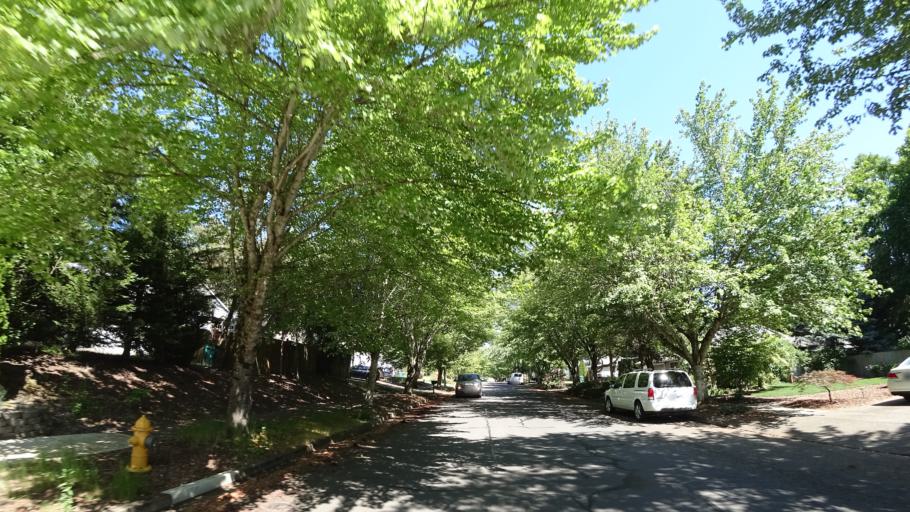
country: US
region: Oregon
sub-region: Washington County
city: Beaverton
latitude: 45.4459
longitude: -122.8138
